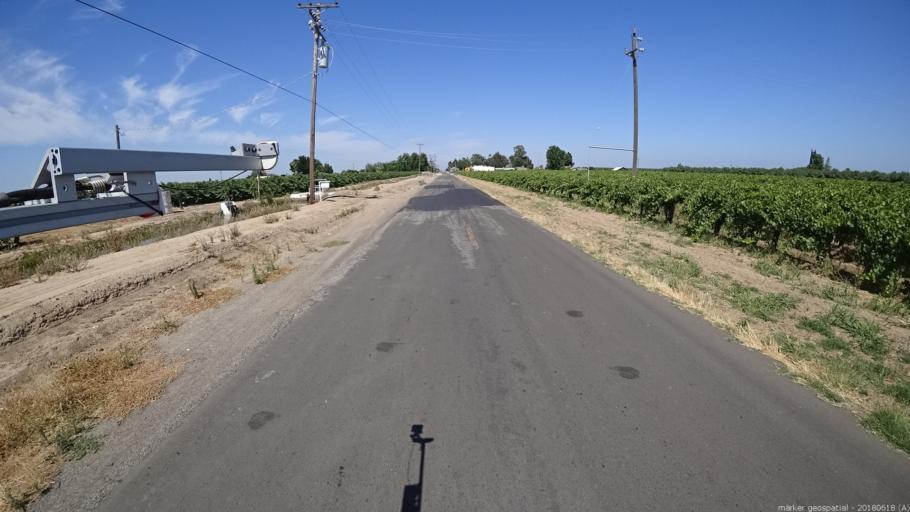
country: US
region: California
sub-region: Madera County
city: Parkwood
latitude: 36.8803
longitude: -120.1068
